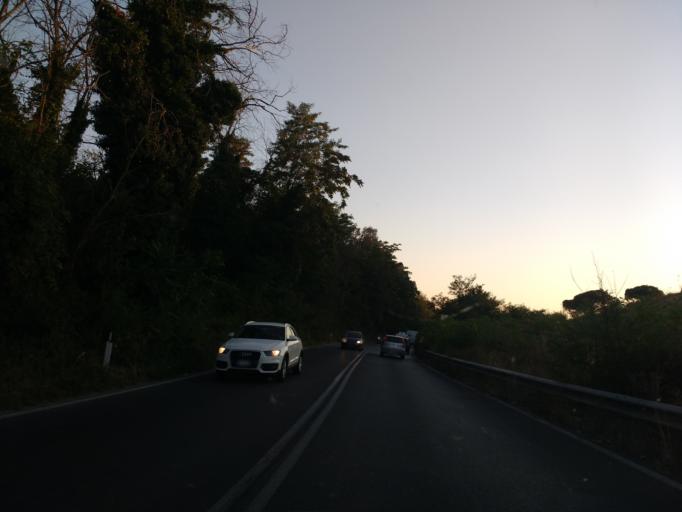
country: IT
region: Latium
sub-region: Citta metropolitana di Roma Capitale
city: Setteville
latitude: 41.9448
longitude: 12.6628
